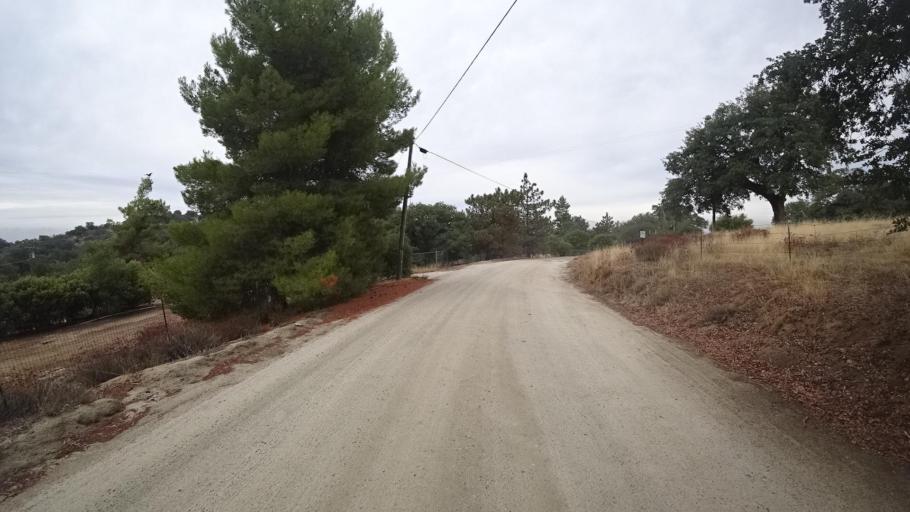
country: US
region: California
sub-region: San Diego County
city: Julian
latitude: 33.0435
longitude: -116.6404
